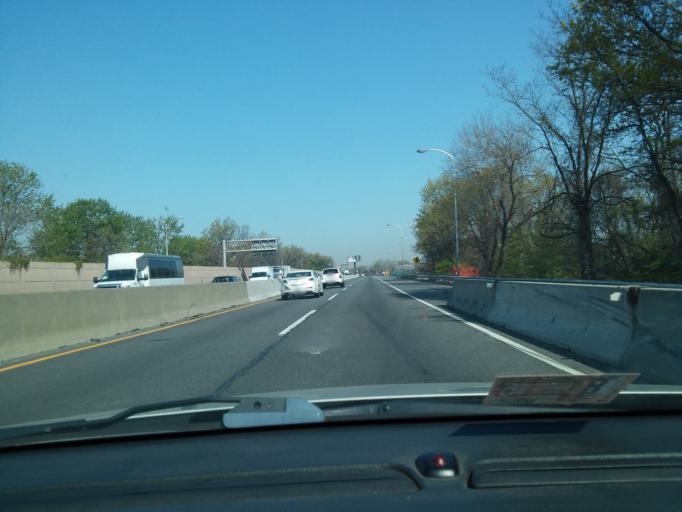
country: US
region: New Jersey
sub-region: Hudson County
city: Bayonne
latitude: 40.6872
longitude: -74.0990
